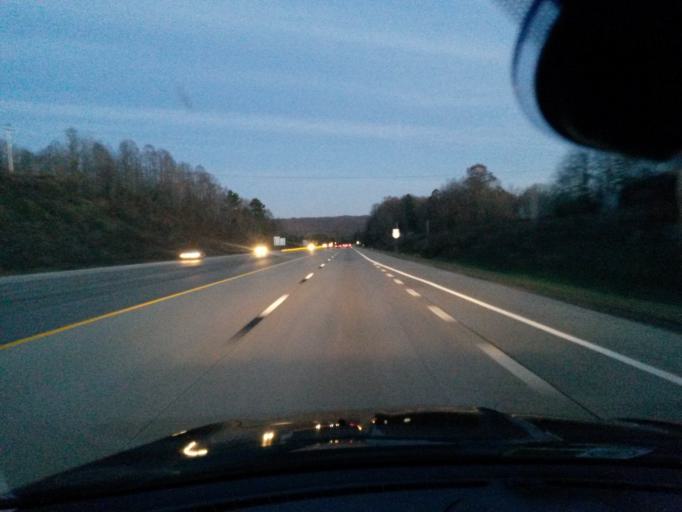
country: US
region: West Virginia
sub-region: Raleigh County
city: Daniels
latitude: 37.7731
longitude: -81.0583
